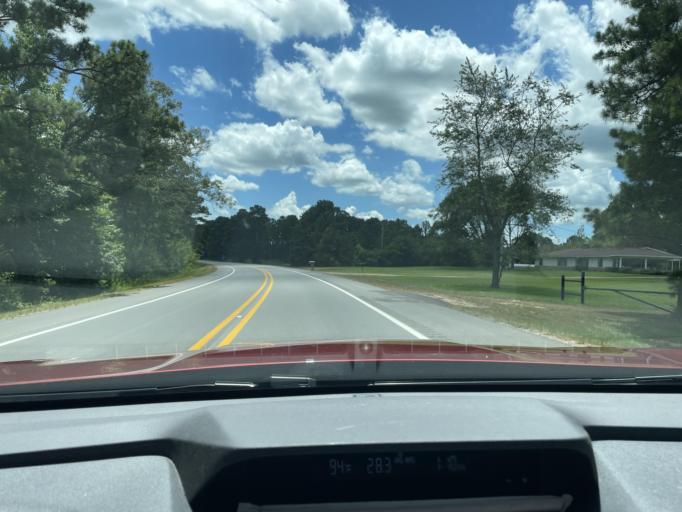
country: US
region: Arkansas
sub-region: Drew County
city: Monticello
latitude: 33.7166
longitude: -91.8112
